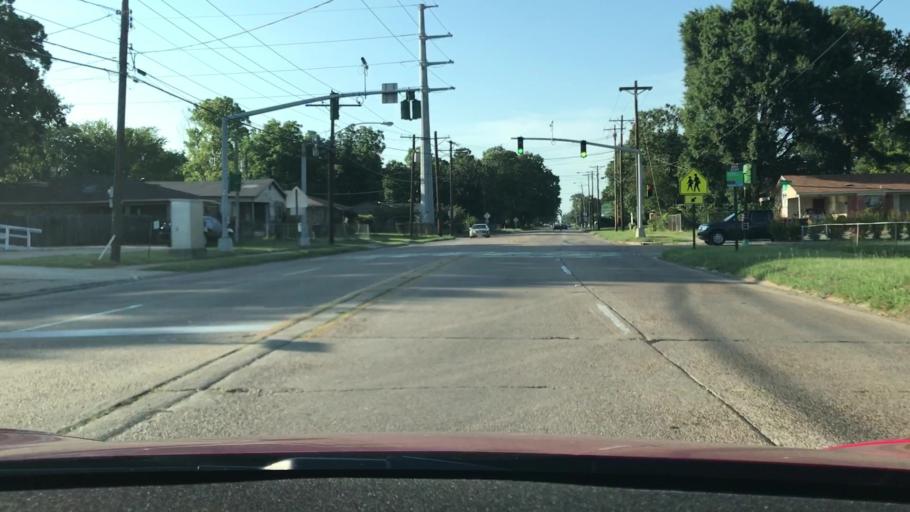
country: US
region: Louisiana
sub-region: Bossier Parish
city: Bossier City
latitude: 32.4329
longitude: -93.7460
